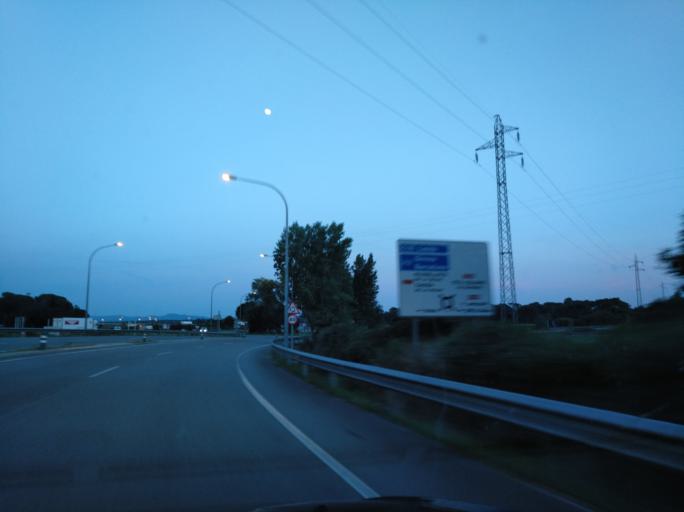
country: ES
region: Catalonia
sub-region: Provincia de Girona
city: Riudellots de la Selva
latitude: 41.8944
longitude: 2.7788
